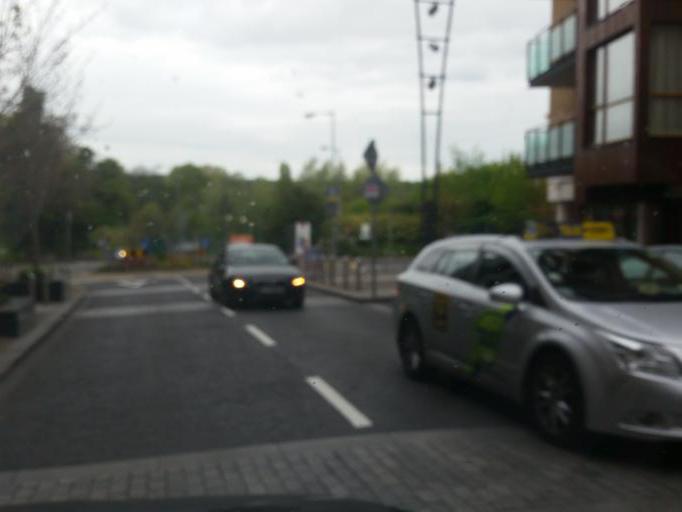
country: IE
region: Leinster
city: Castleknock
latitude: 53.3762
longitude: -6.3328
